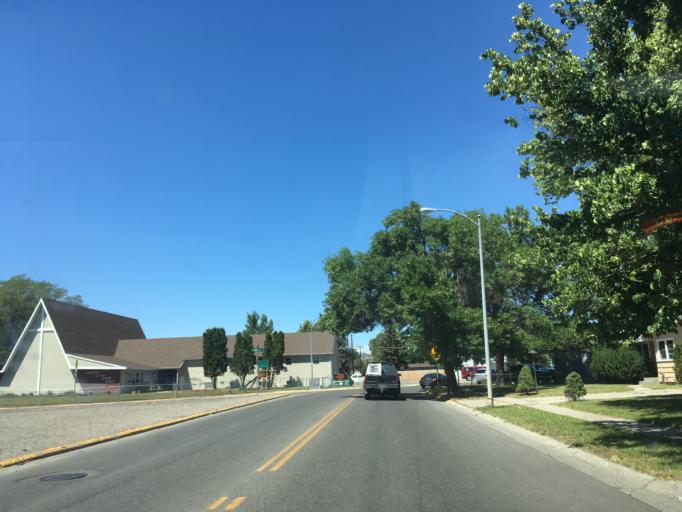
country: US
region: Montana
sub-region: Yellowstone County
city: Billings
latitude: 45.7723
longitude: -108.5647
